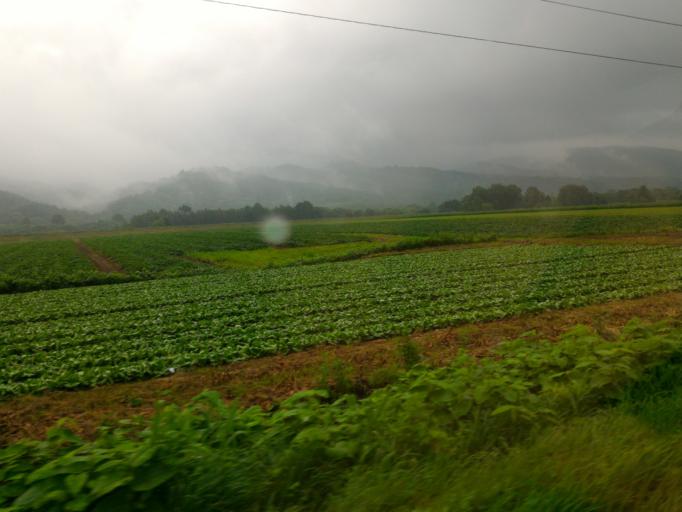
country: JP
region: Hokkaido
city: Nayoro
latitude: 44.5872
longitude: 142.3064
